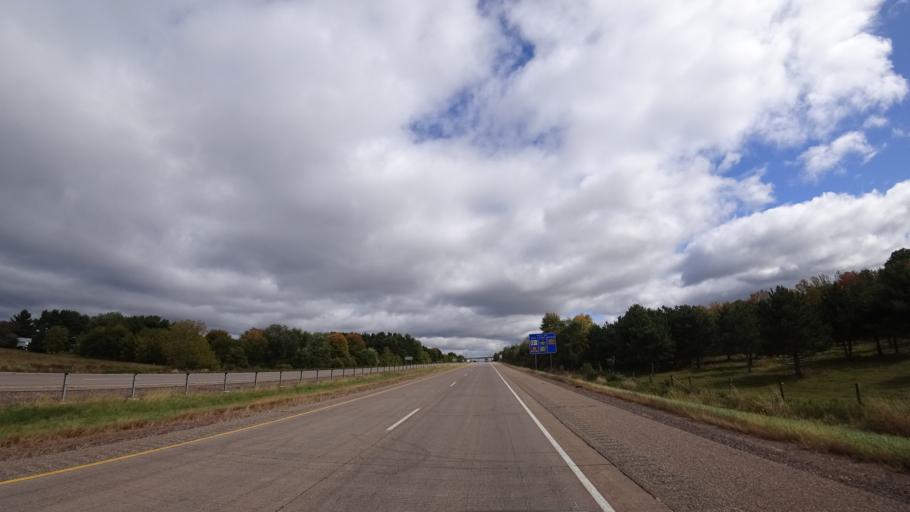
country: US
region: Wisconsin
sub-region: Chippewa County
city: Chippewa Falls
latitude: 44.9199
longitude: -91.3539
